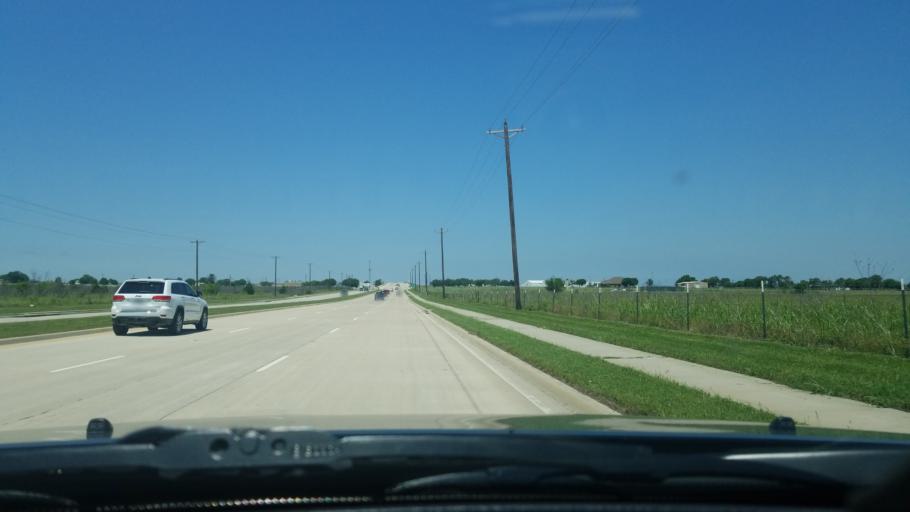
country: US
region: Texas
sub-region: Denton County
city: Krum
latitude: 33.2342
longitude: -97.2372
